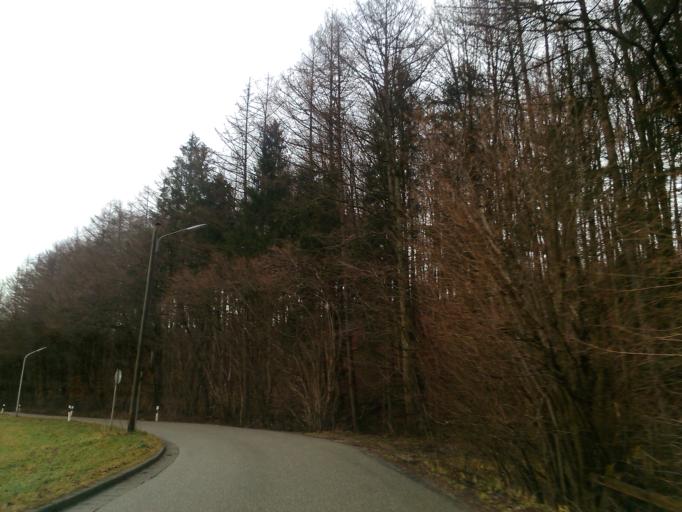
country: DE
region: Bavaria
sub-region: Upper Bavaria
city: Starnberg
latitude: 48.0302
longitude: 11.3548
